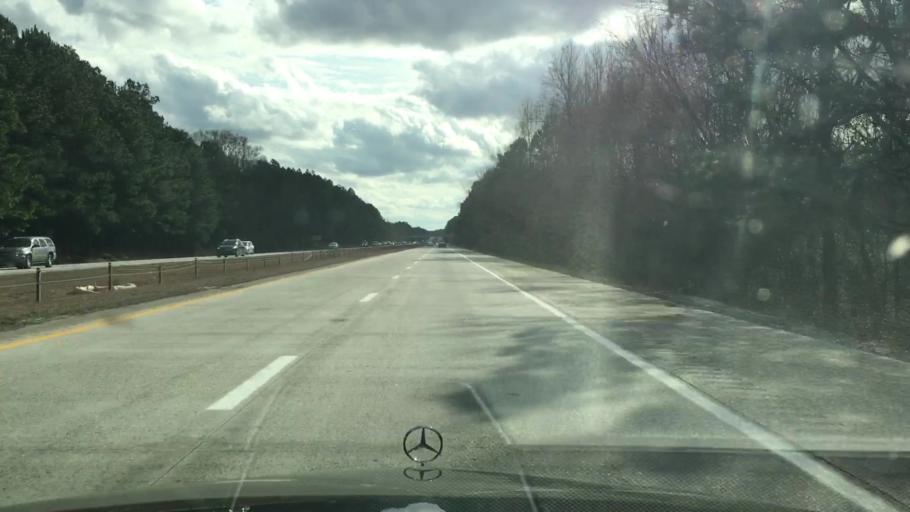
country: US
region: North Carolina
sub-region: Johnston County
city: Benson
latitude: 35.4969
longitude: -78.5536
